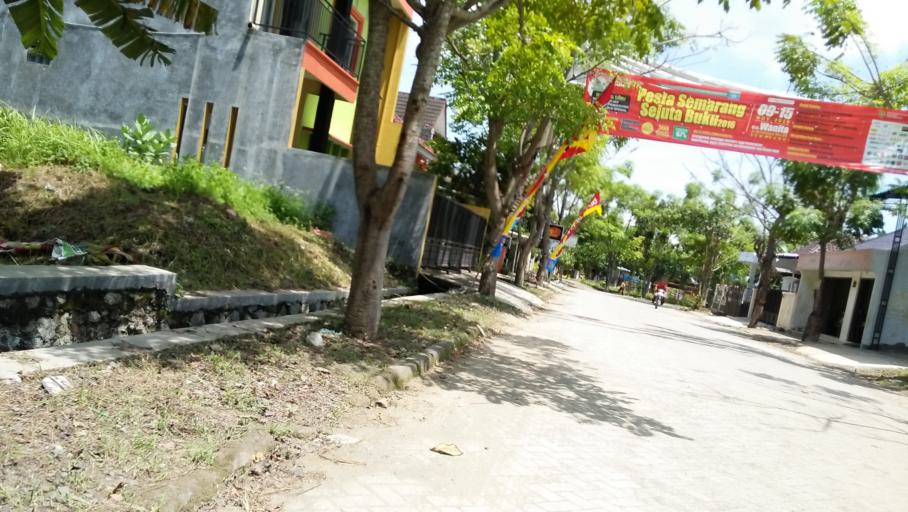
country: ID
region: Central Java
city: Mranggen
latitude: -7.0596
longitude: 110.4702
